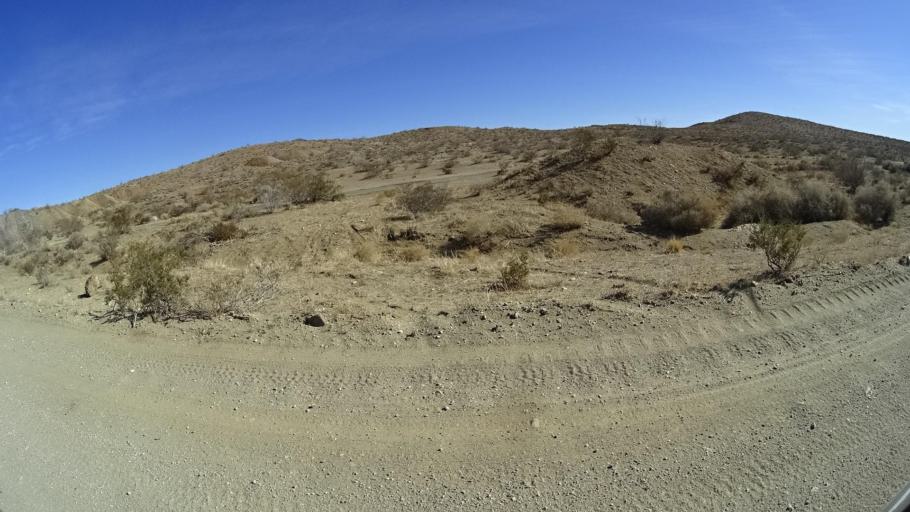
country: US
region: California
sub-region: Kern County
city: Ridgecrest
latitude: 35.3388
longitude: -117.6323
